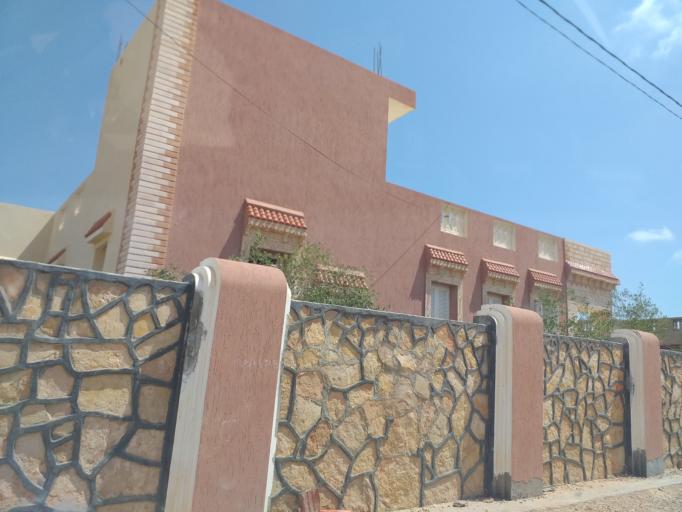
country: TN
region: Qabis
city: Gabes
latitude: 33.9474
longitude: 10.0590
